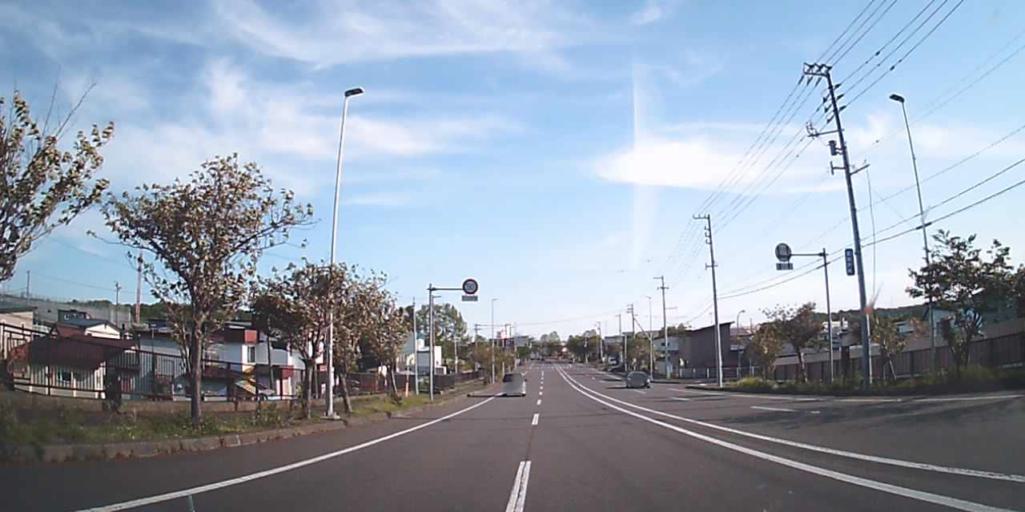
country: JP
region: Hokkaido
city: Shiraoi
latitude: 42.4583
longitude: 141.1774
